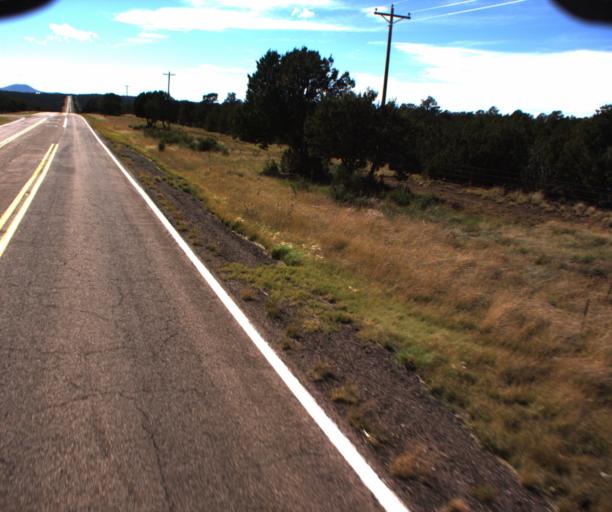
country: US
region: Arizona
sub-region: Navajo County
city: White Mountain Lake
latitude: 34.3064
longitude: -109.7790
